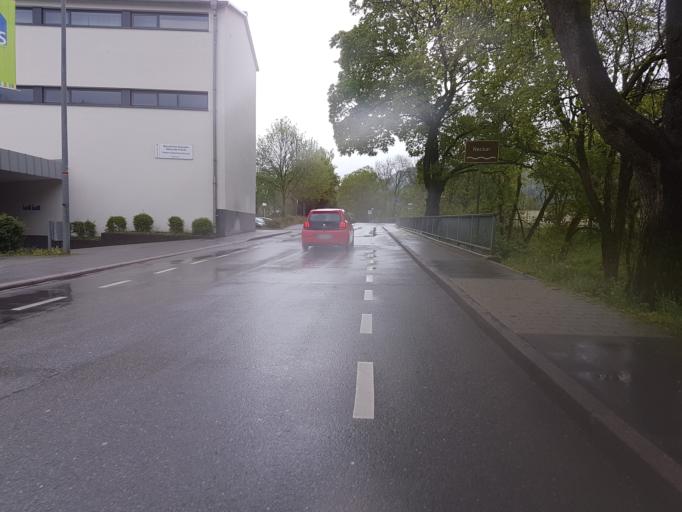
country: DE
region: Baden-Wuerttemberg
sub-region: Freiburg Region
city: Oberndorf
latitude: 48.2885
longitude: 8.5797
